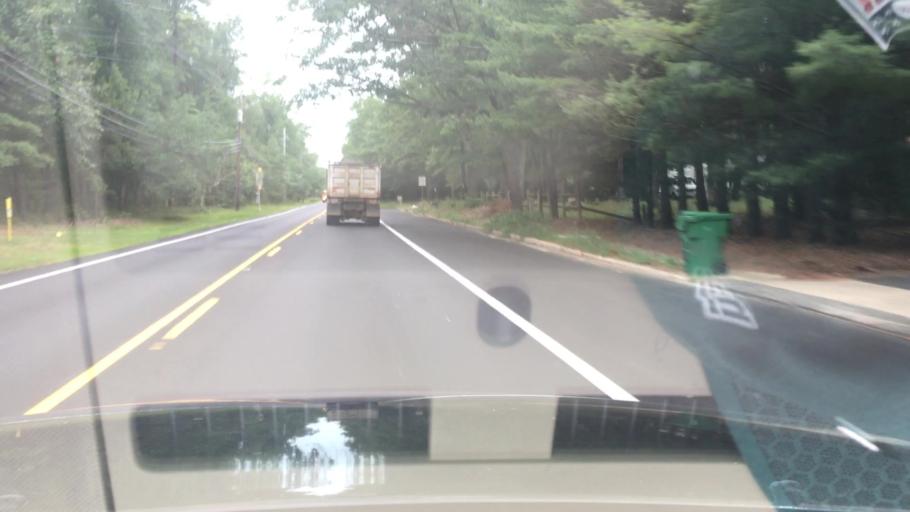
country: US
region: New Jersey
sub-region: Ocean County
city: Lakehurst
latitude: 40.0595
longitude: -74.3540
